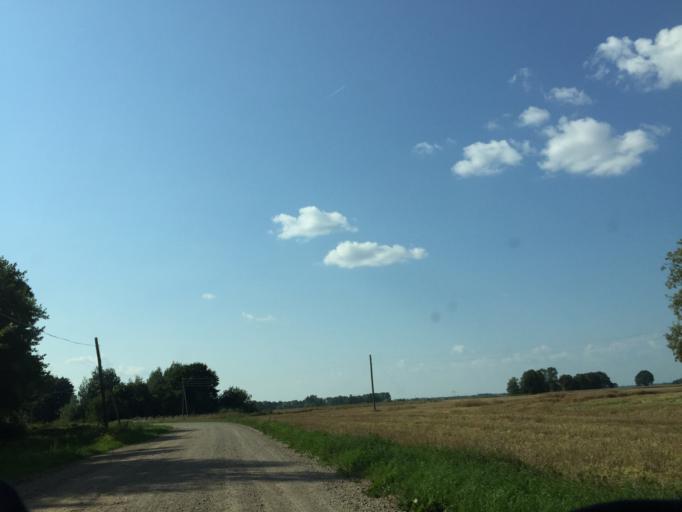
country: LV
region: Jelgava
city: Jelgava
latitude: 56.4531
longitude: 23.7378
